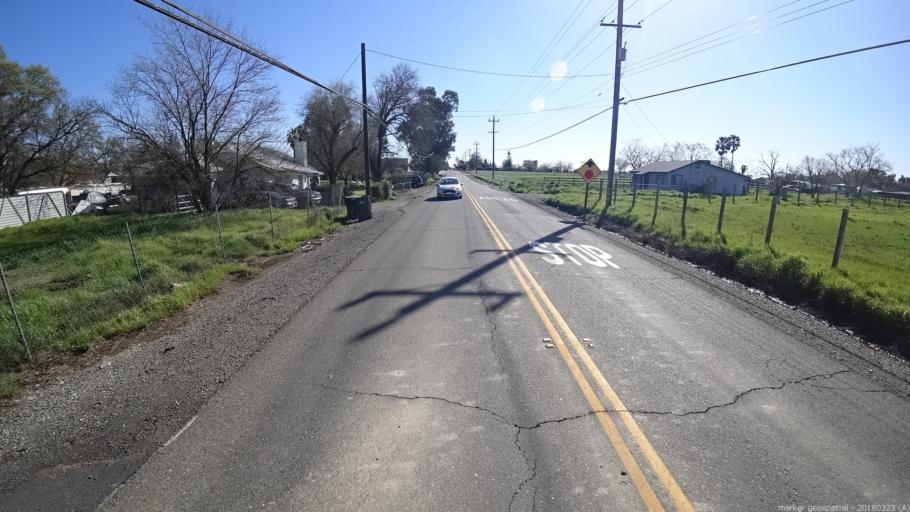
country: US
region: California
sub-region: Sacramento County
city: Rio Linda
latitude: 38.6979
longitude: -121.4123
